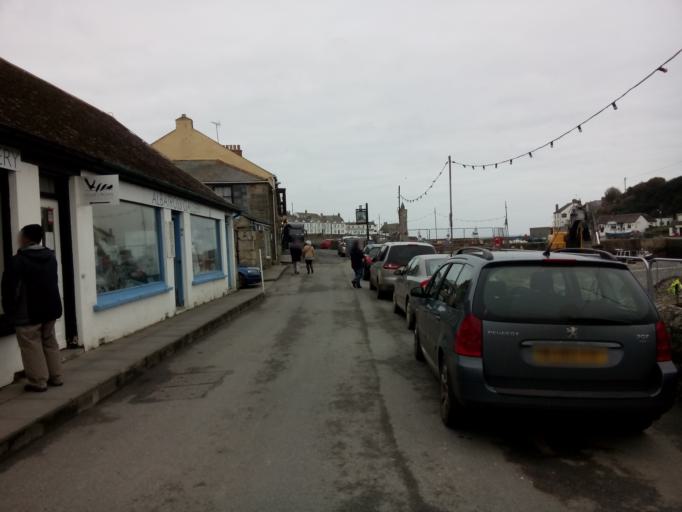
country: GB
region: England
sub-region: Cornwall
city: Porthleven
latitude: 50.0850
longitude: -5.3161
